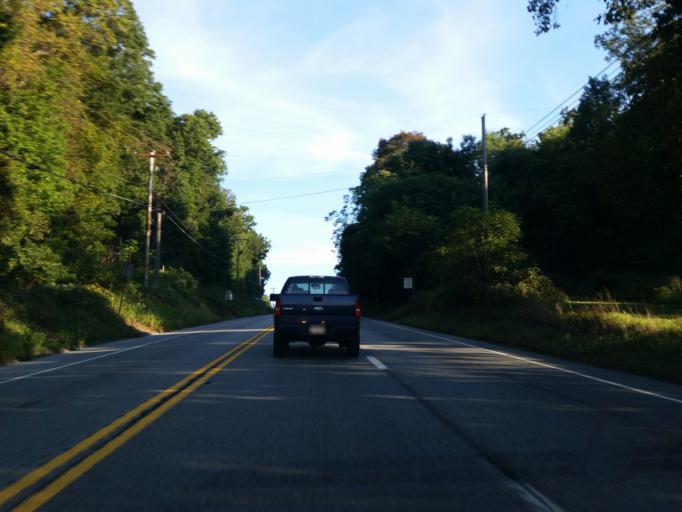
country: US
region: Pennsylvania
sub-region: Lancaster County
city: Quarryville
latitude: 39.8742
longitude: -76.2291
